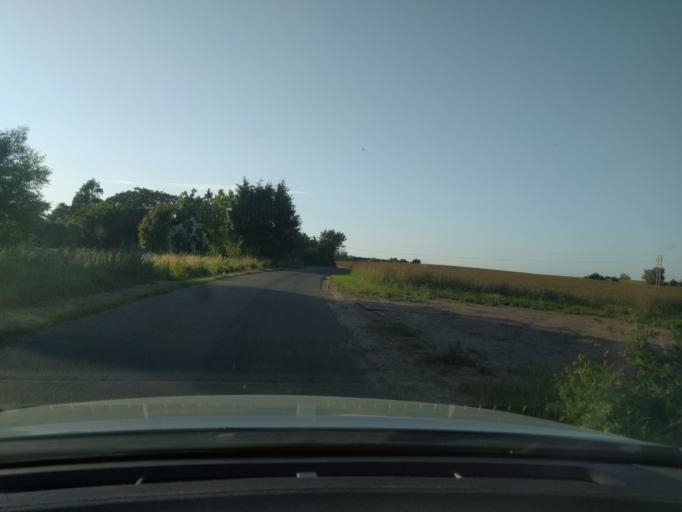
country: DK
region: Zealand
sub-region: Vordingborg Kommune
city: Stege
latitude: 54.9617
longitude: 12.2365
